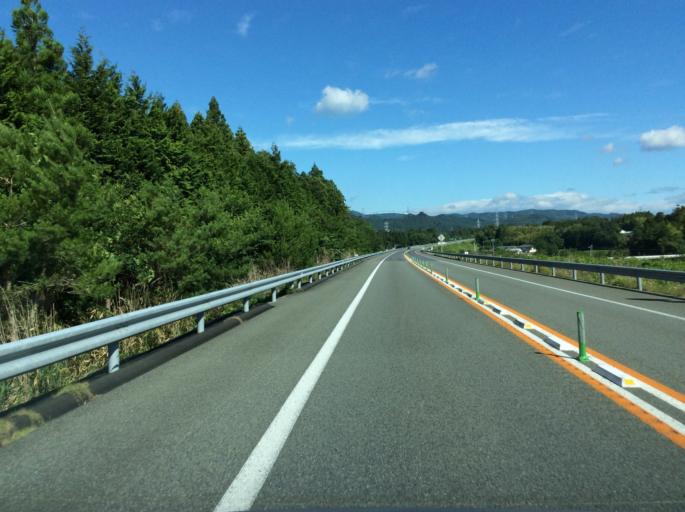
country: JP
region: Fukushima
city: Namie
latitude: 37.3521
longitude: 140.9799
